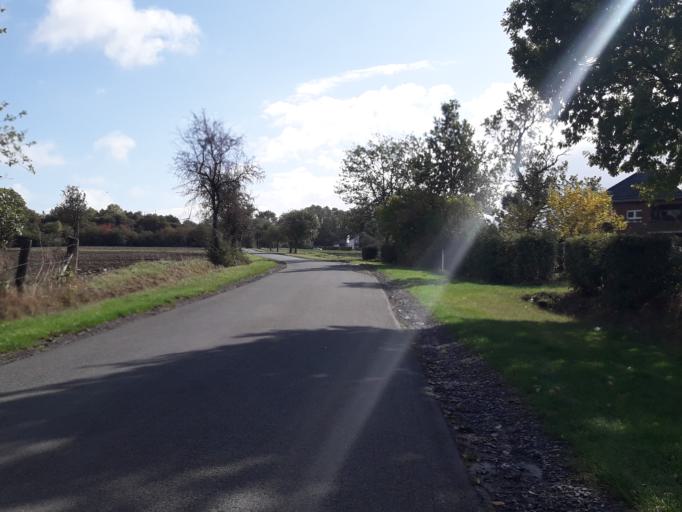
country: DE
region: North Rhine-Westphalia
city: Bad Lippspringe
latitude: 51.7403
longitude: 8.8072
